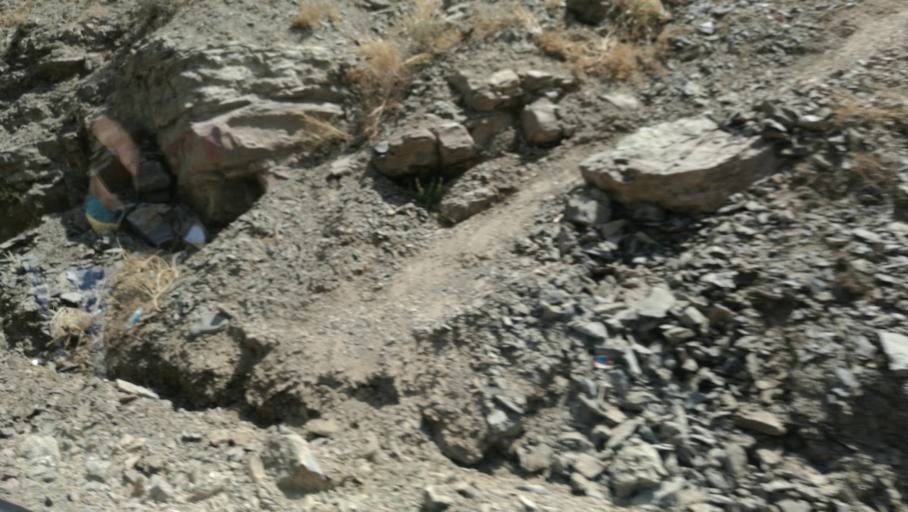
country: IR
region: Alborz
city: Karaj
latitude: 35.9396
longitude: 51.0727
